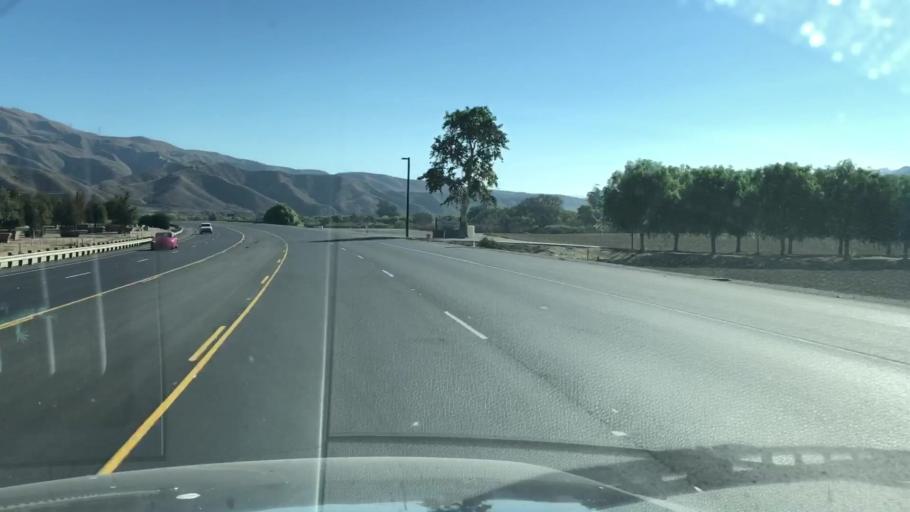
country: US
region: California
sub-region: Ventura County
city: Piru
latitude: 34.4053
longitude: -118.7416
